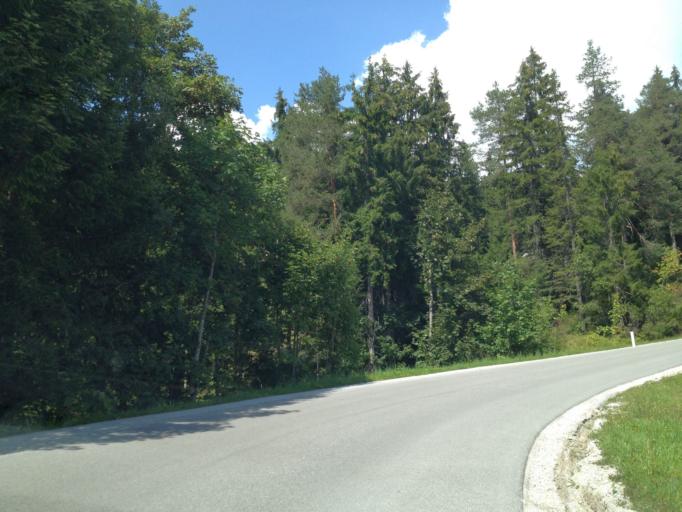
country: AT
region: Styria
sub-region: Politischer Bezirk Liezen
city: Schladming
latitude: 47.4034
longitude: 13.6199
